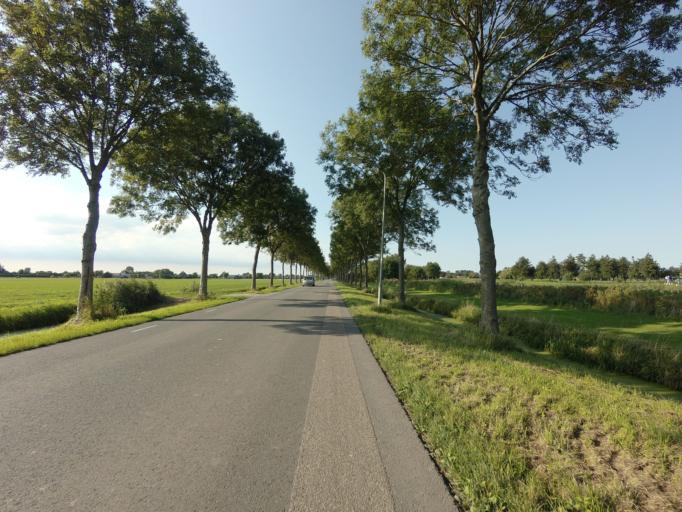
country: NL
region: North Holland
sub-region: Gemeente Hoorn
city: Hoorn
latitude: 52.6722
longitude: 5.1397
